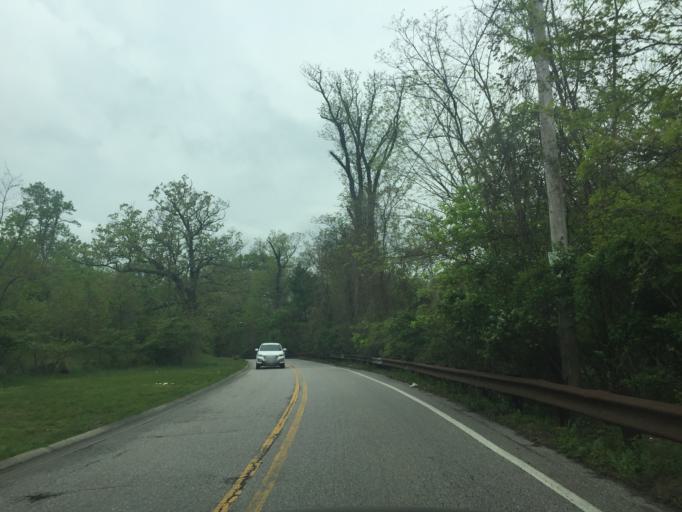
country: US
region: Maryland
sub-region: Baltimore County
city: Charlestown
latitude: 39.3059
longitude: -76.6807
